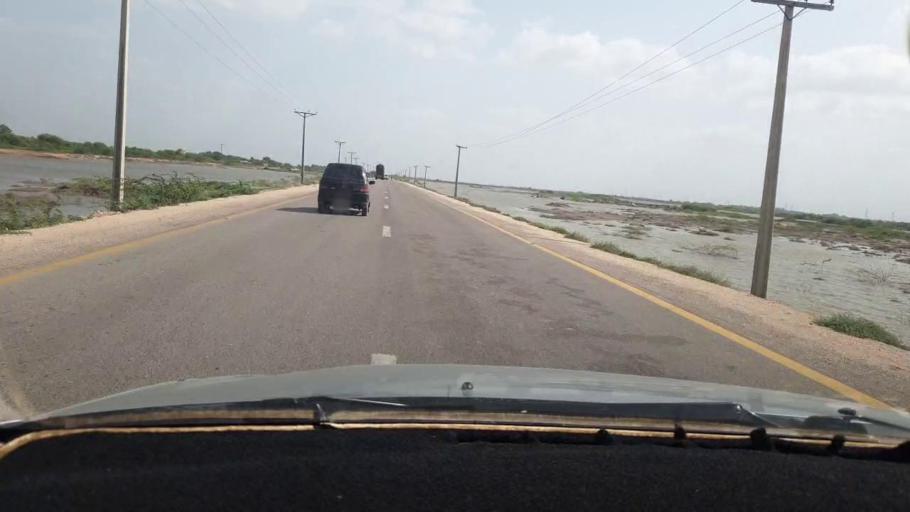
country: PK
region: Sindh
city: Naukot
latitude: 24.9337
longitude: 69.3155
